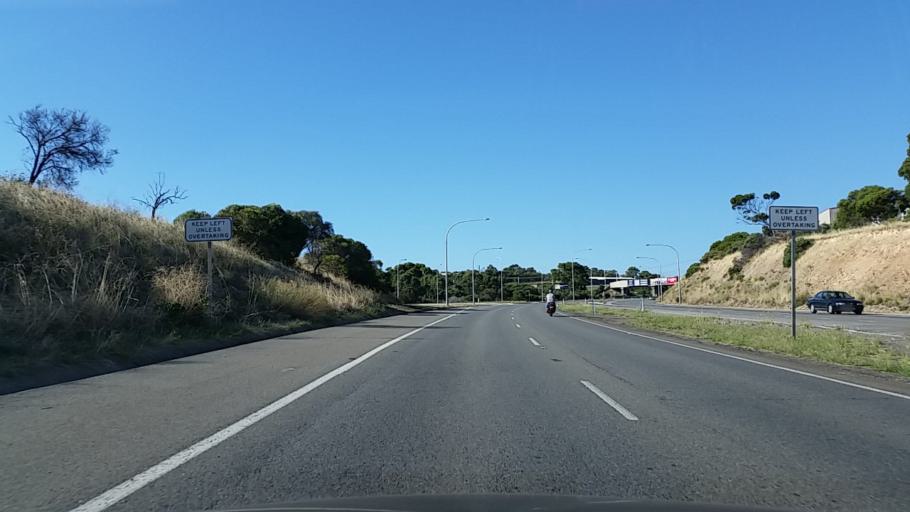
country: AU
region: South Australia
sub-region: Onkaparinga
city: Morphett Vale
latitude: -35.1147
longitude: 138.4912
